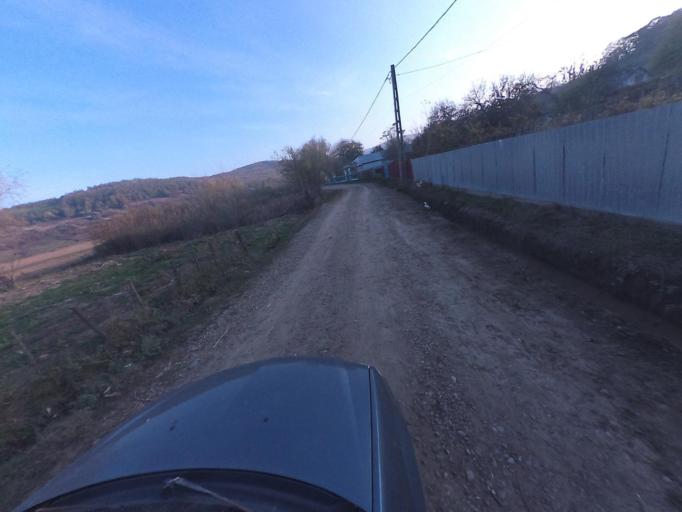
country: RO
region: Vaslui
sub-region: Comuna Bacesti
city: Bacesti
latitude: 46.7995
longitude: 27.2251
